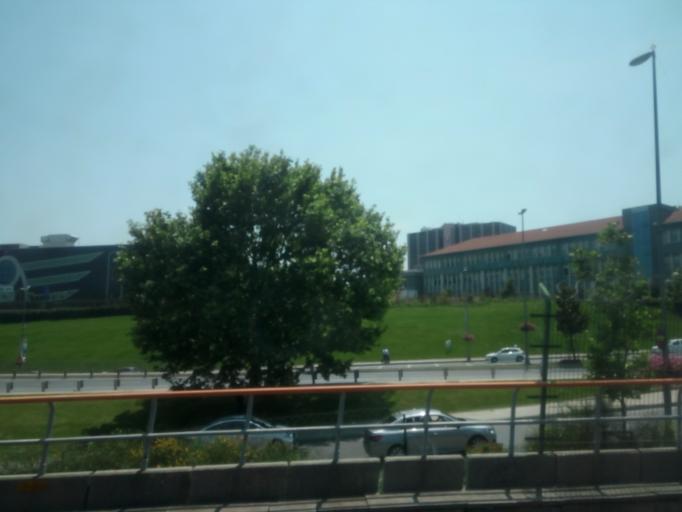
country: TR
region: Istanbul
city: Bahcelievler
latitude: 40.9854
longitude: 28.8248
